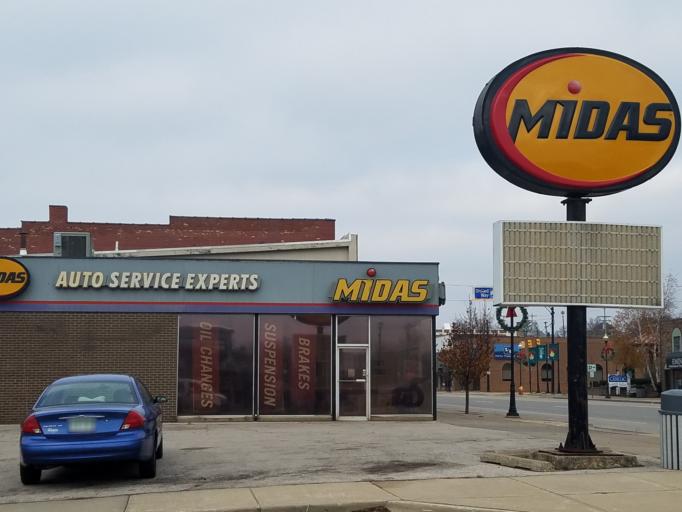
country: US
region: Michigan
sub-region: Wexford County
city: Cadillac
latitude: 44.2483
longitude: -85.3980
